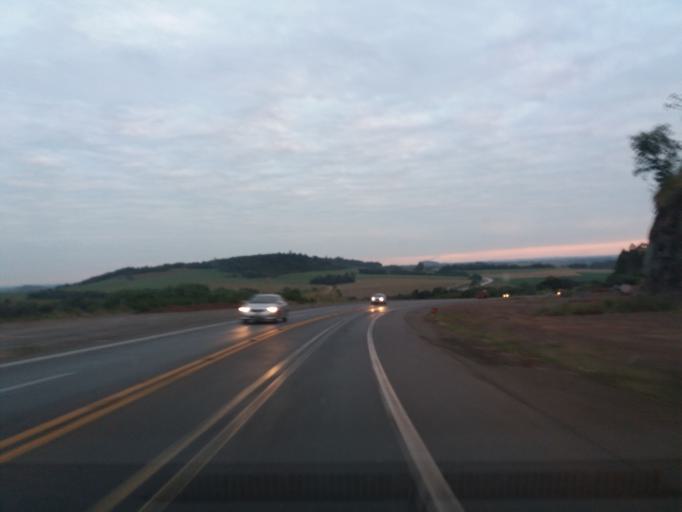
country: BR
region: Parana
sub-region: Realeza
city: Realeza
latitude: -25.3761
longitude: -53.5748
